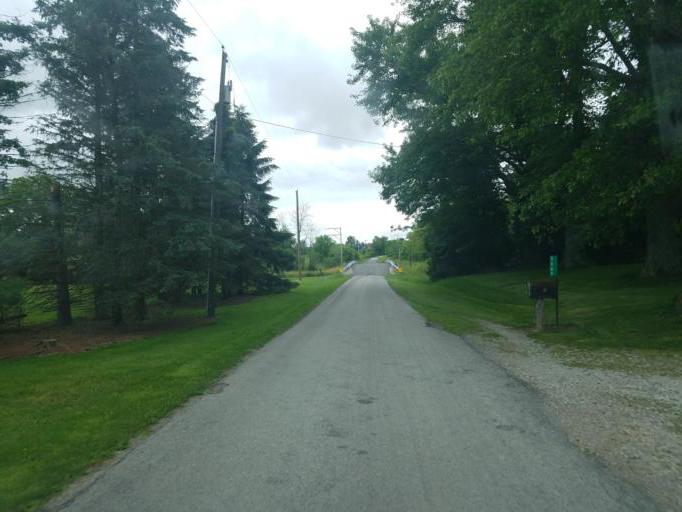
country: US
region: Ohio
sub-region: Morrow County
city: Cardington
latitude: 40.5459
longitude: -82.9135
